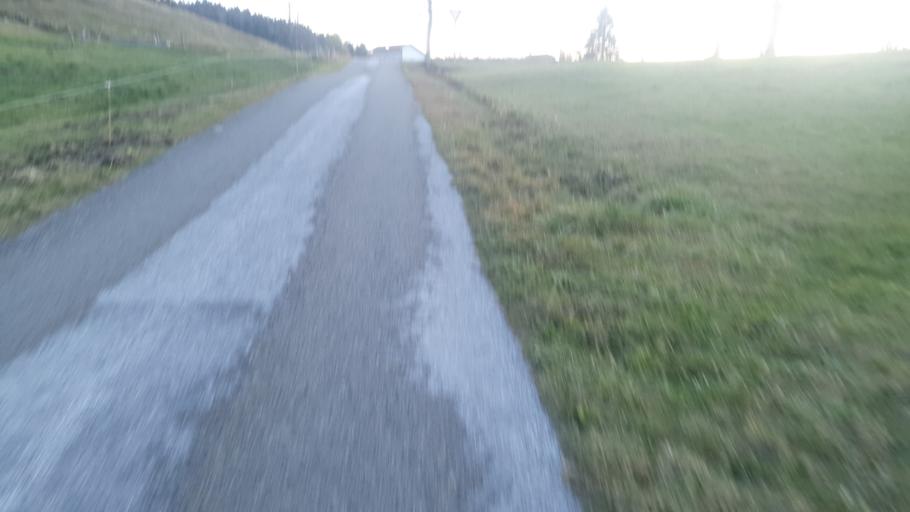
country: FR
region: Franche-Comte
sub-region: Departement du Jura
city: Saint-Claude
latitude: 46.3041
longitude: 5.8537
